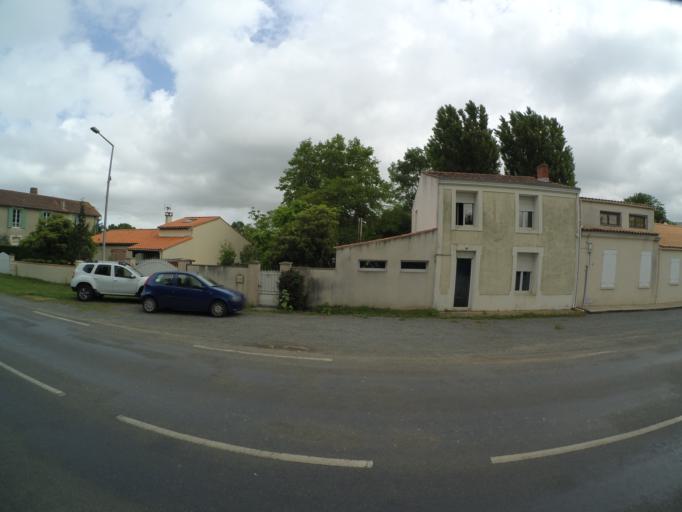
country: FR
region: Poitou-Charentes
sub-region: Departement de la Charente-Maritime
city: Saint-Laurent-de-la-Pree
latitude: 45.9932
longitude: -1.0299
